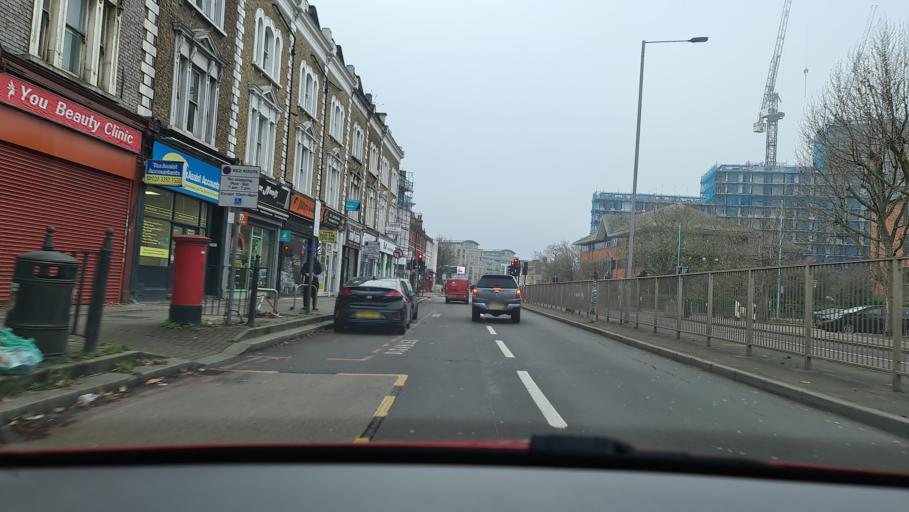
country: GB
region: England
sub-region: Greater London
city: Acton
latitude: 51.4906
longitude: -0.2845
